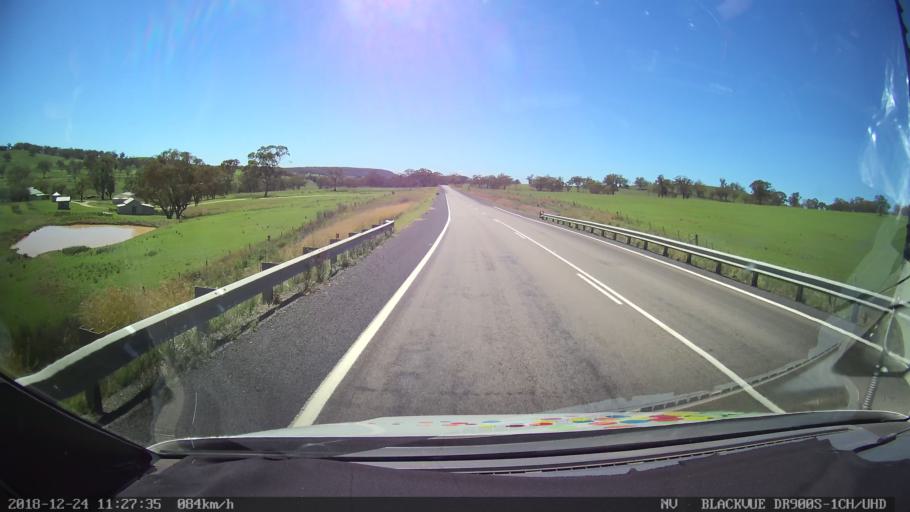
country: AU
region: New South Wales
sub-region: Upper Hunter Shire
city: Merriwa
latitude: -32.1835
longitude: 150.4363
